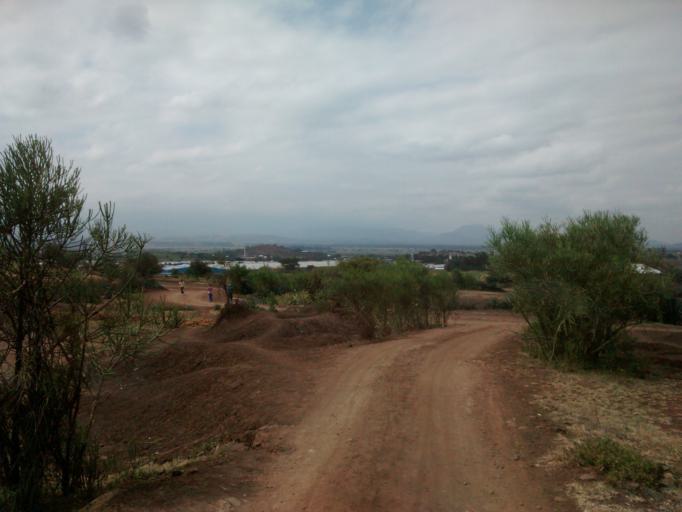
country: TZ
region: Arusha
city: Arusha
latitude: -3.3920
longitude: 36.5904
